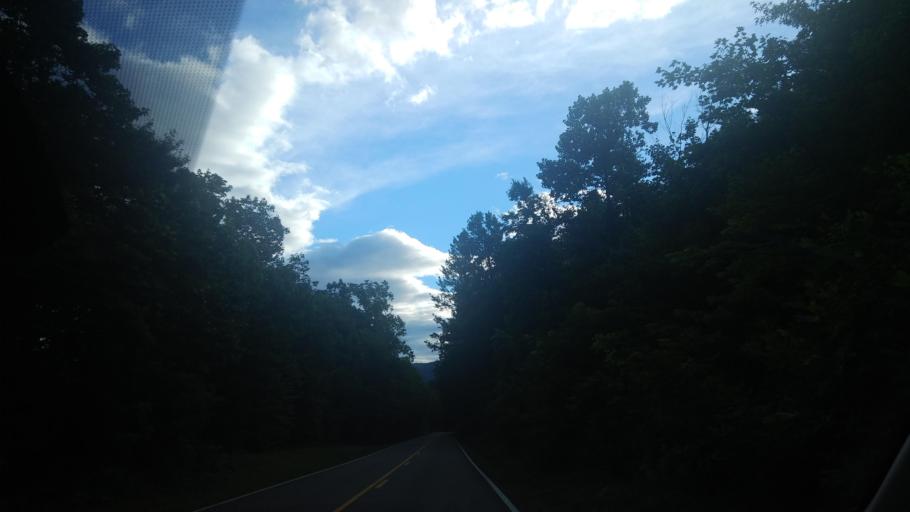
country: US
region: Tennessee
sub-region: Cocke County
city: Newport
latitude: 35.8250
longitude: -83.2034
